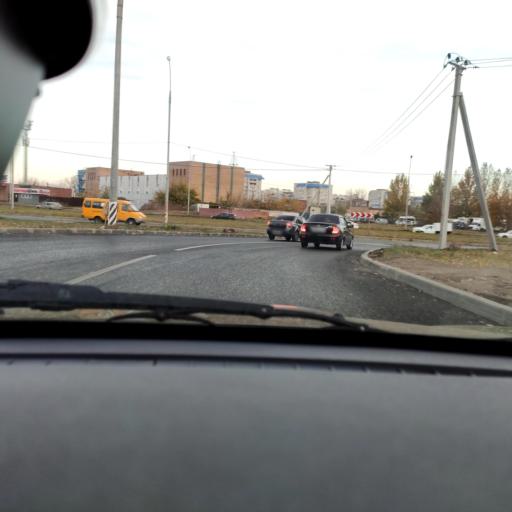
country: RU
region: Samara
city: Tol'yatti
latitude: 53.5434
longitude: 49.3199
